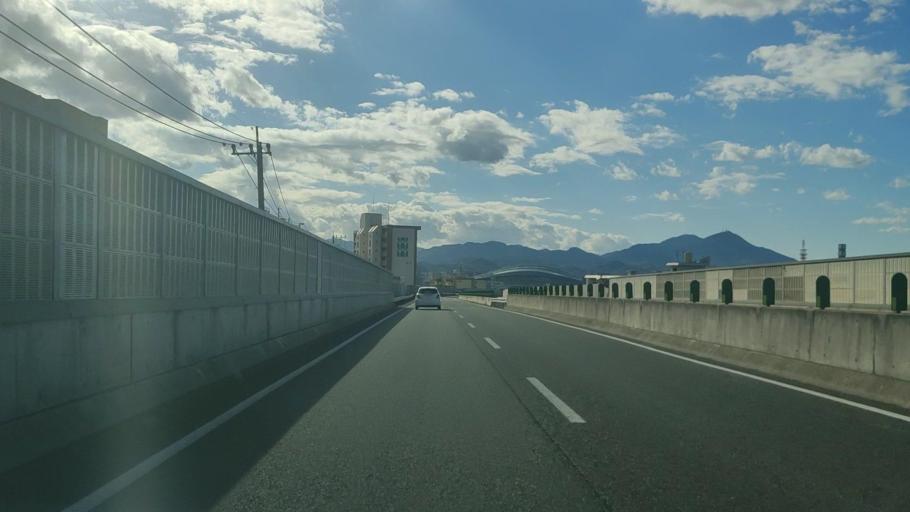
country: JP
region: Yamaguchi
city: Shimonoseki
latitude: 33.8812
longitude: 130.9039
